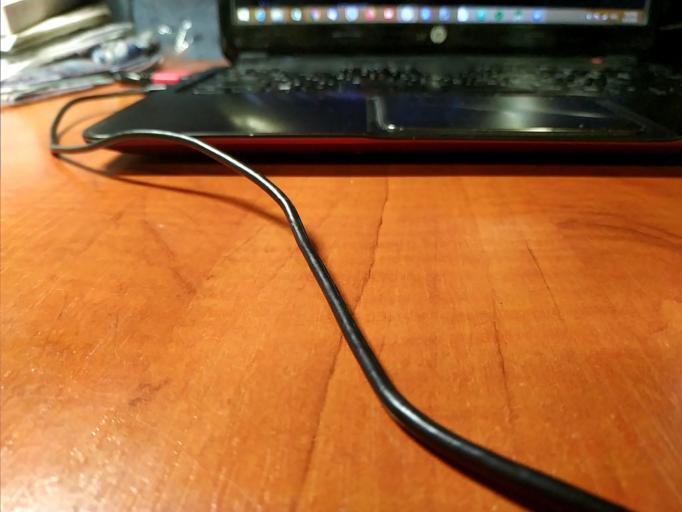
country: RU
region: Tverskaya
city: Zubtsov
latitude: 56.3133
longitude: 34.6798
